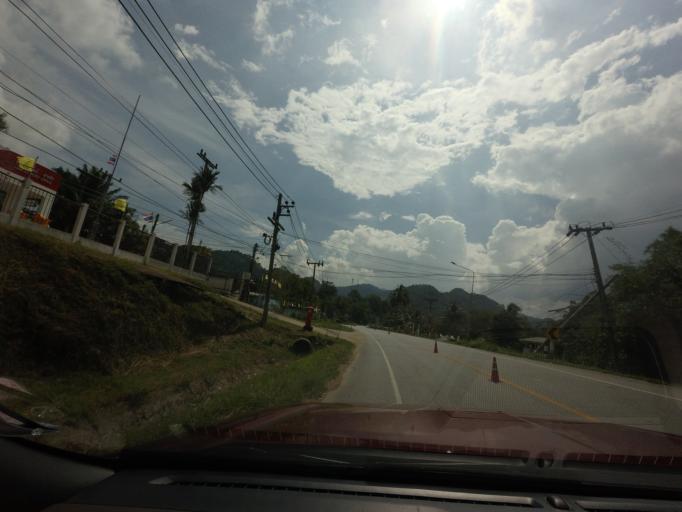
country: TH
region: Yala
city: Than To
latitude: 6.1609
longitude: 101.1873
